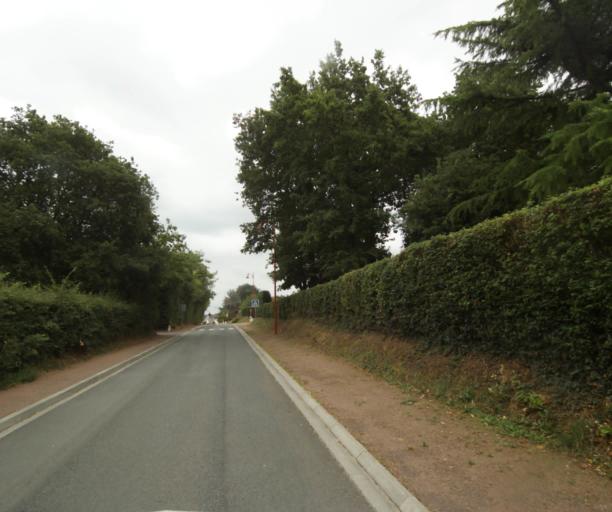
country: FR
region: Pays de la Loire
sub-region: Departement de la Sarthe
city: Solesmes
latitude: 47.8520
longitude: -0.2957
